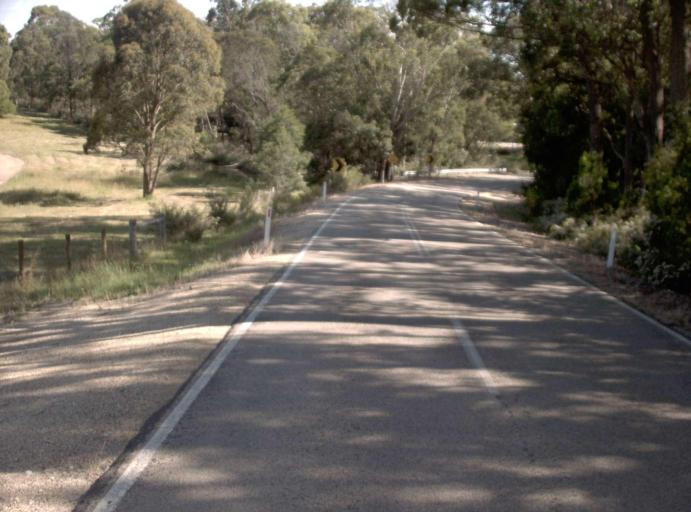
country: AU
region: Victoria
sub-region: East Gippsland
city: Lakes Entrance
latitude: -37.7570
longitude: 147.8144
